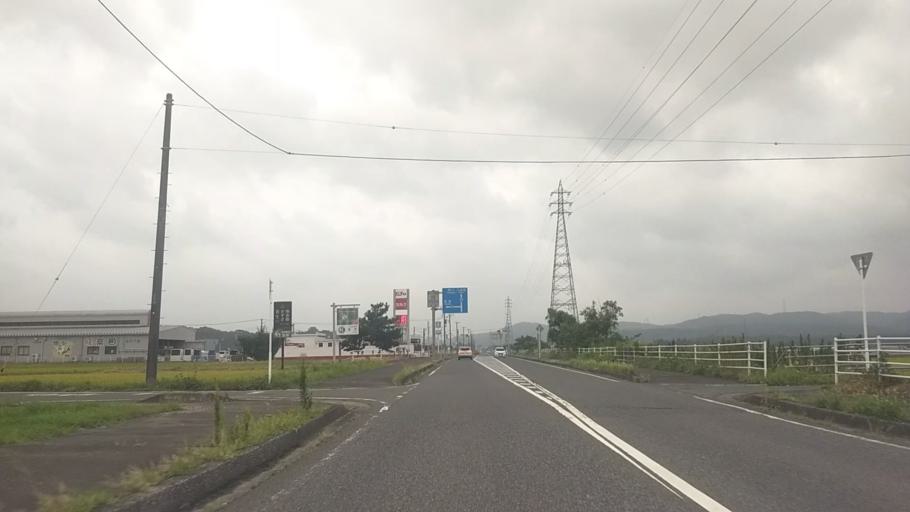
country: JP
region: Chiba
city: Kisarazu
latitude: 35.3322
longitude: 140.0550
